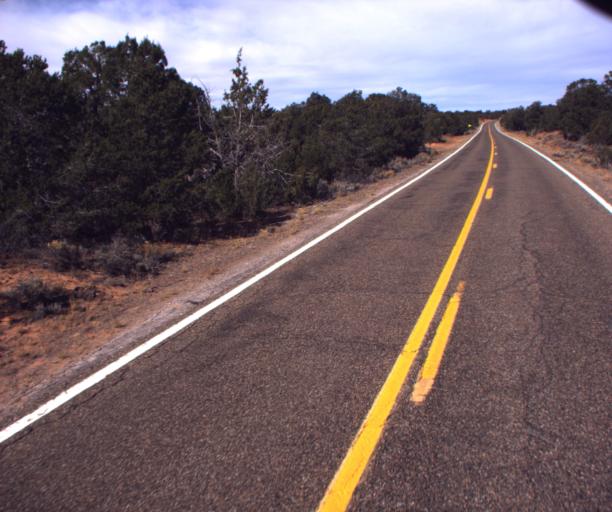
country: US
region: Arizona
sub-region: Navajo County
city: Kayenta
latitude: 36.6415
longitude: -110.5128
